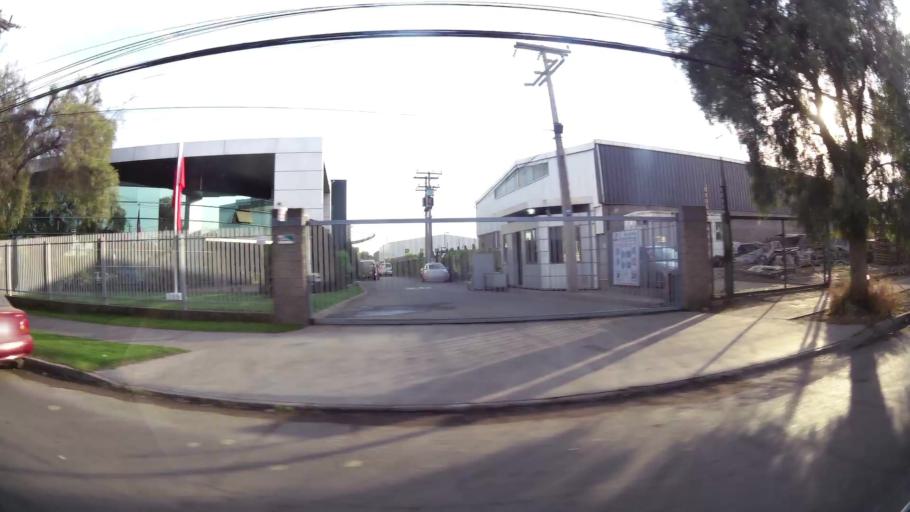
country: CL
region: Santiago Metropolitan
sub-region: Provincia de Maipo
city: San Bernardo
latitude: -33.5572
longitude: -70.7192
